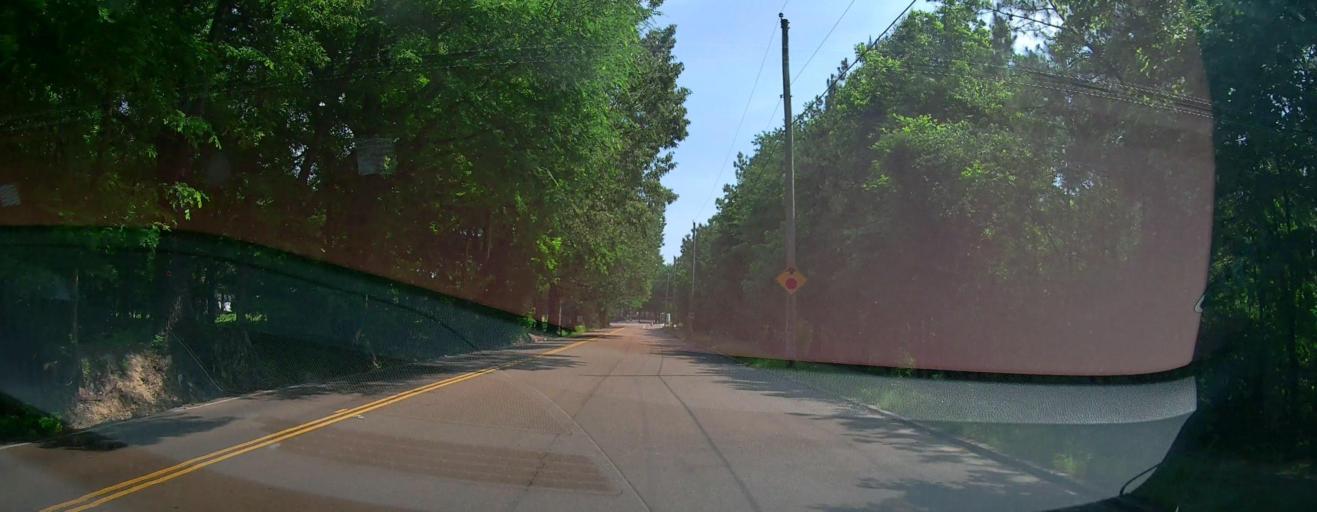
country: US
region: Mississippi
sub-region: De Soto County
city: Olive Branch
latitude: 35.0078
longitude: -89.8294
